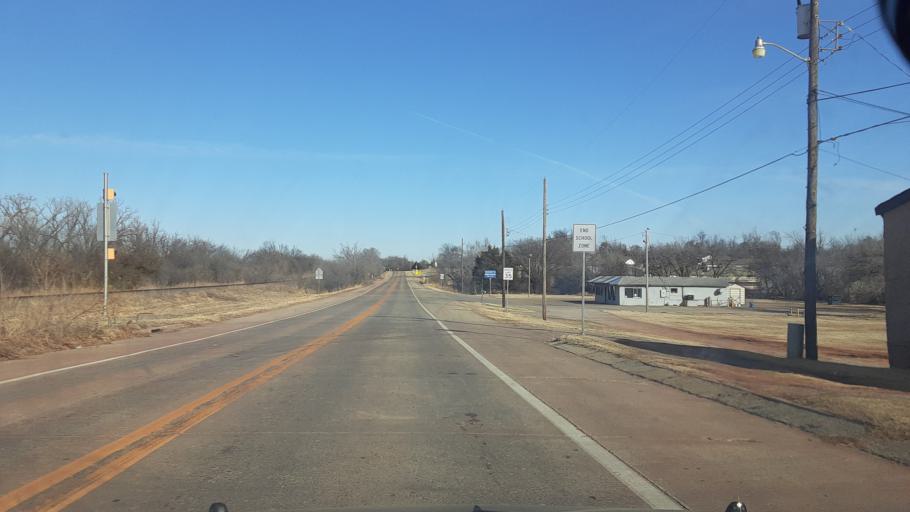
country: US
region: Oklahoma
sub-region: Logan County
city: Guthrie
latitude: 35.8880
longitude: -97.4240
